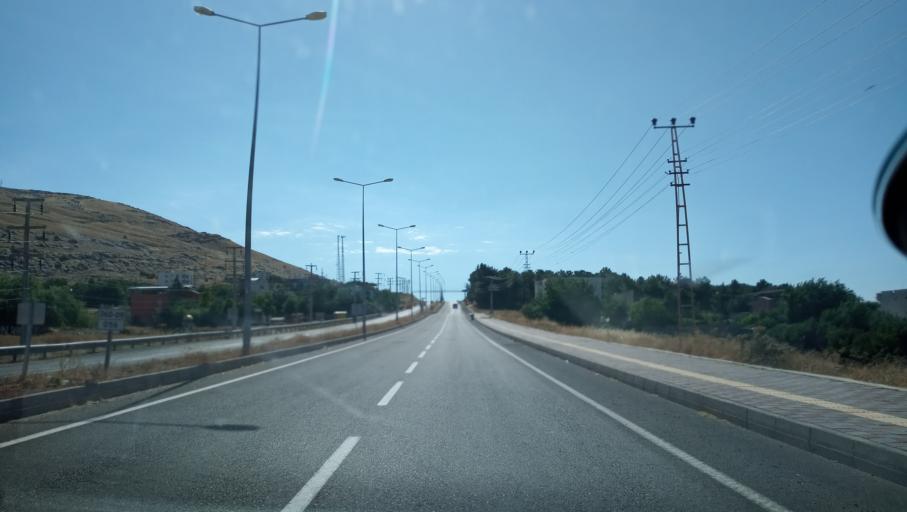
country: TR
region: Diyarbakir
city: Silvan
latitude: 38.1344
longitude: 41.0353
